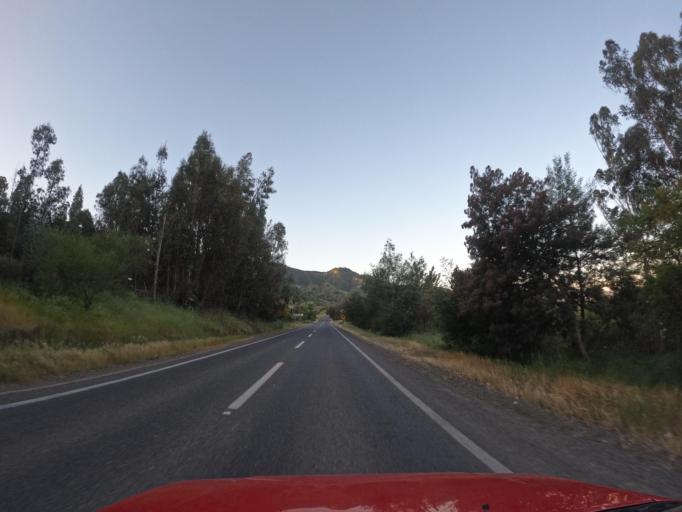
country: CL
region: Maule
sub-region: Provincia de Curico
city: Rauco
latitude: -35.0706
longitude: -71.6251
